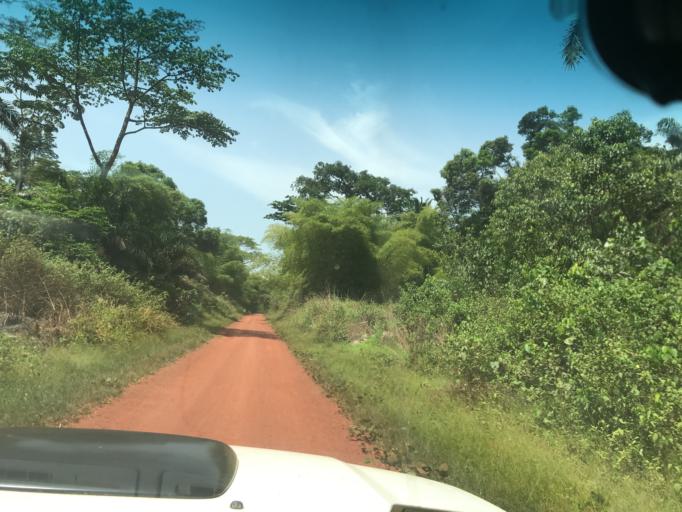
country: CD
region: Eastern Province
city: Aketi
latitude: 2.8851
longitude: 23.9744
